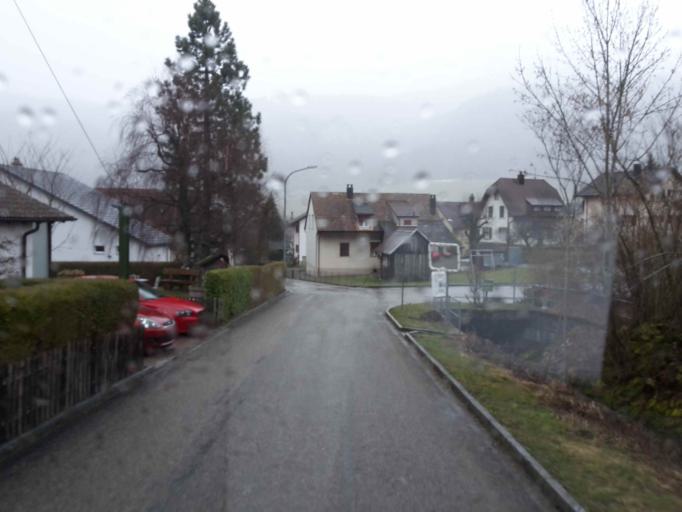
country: CH
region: Solothurn
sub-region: Bezirk Thal
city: Welschenrohr
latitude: 47.2819
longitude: 7.5221
